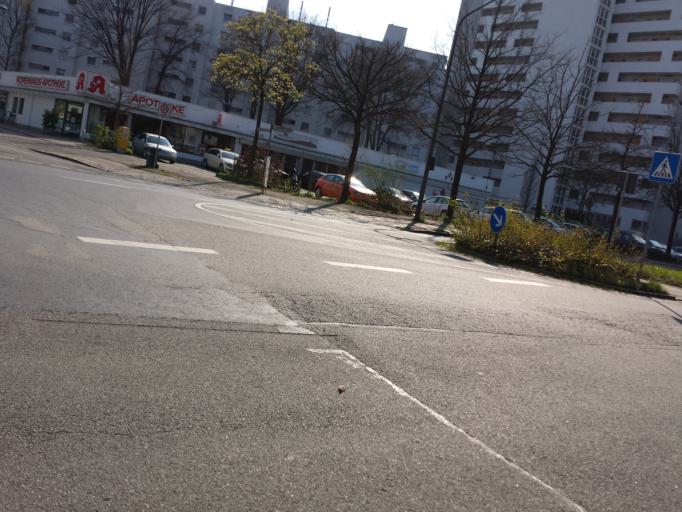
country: DE
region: Lower Saxony
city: Lilienthal
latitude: 53.0863
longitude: 8.8910
